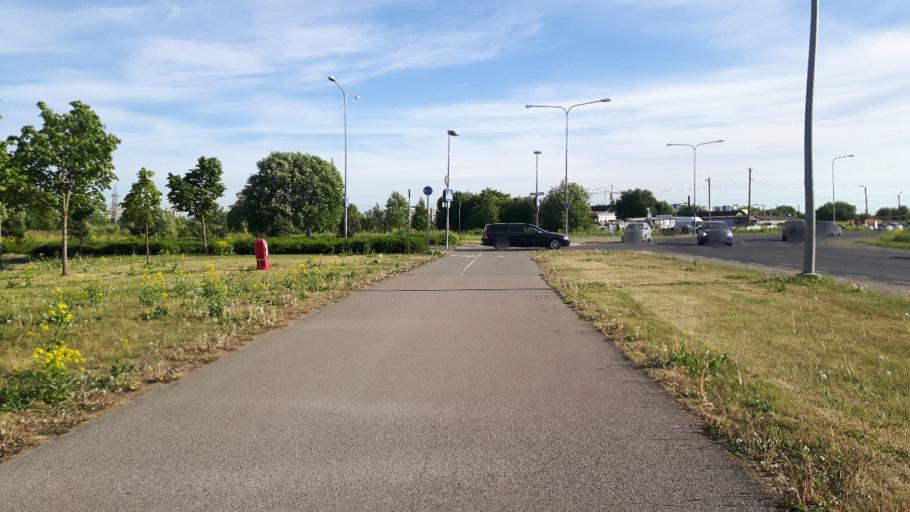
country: EE
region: Harju
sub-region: Tallinna linn
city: Kose
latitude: 59.4501
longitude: 24.8332
